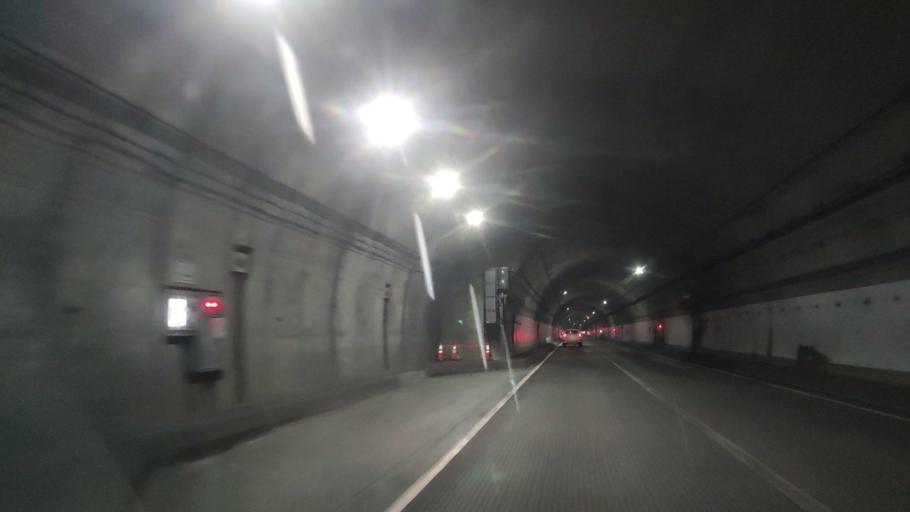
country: JP
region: Hokkaido
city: Rumoi
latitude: 43.7048
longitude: 141.3354
